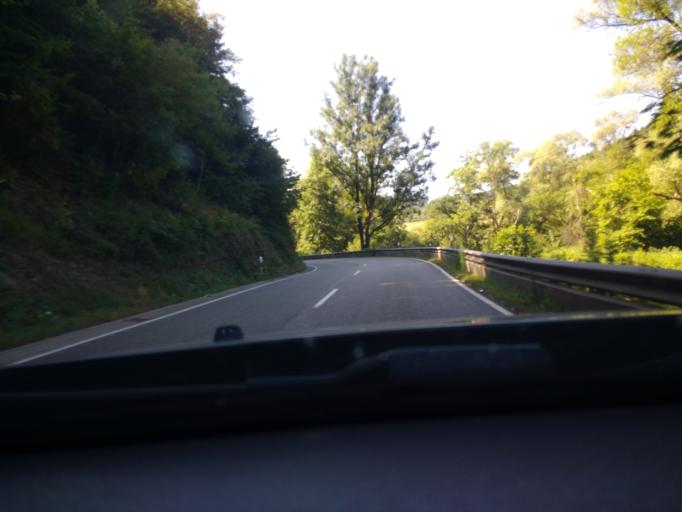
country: DE
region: Rheinland-Pfalz
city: Alf
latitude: 50.0480
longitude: 7.1053
